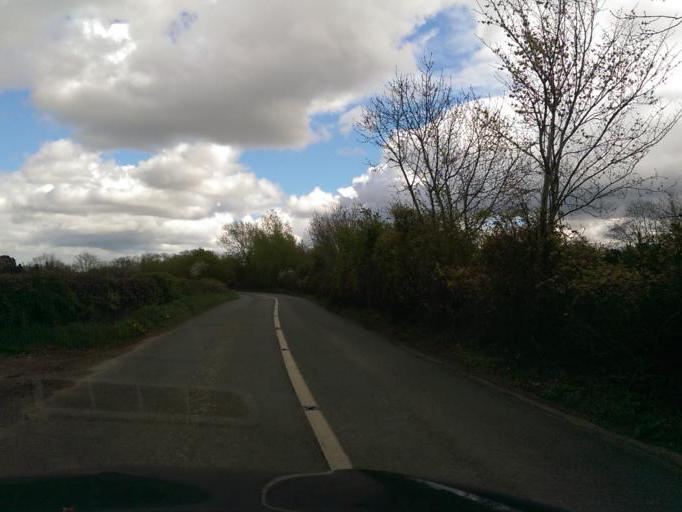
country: IE
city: Confey
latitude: 53.3743
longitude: -6.4755
